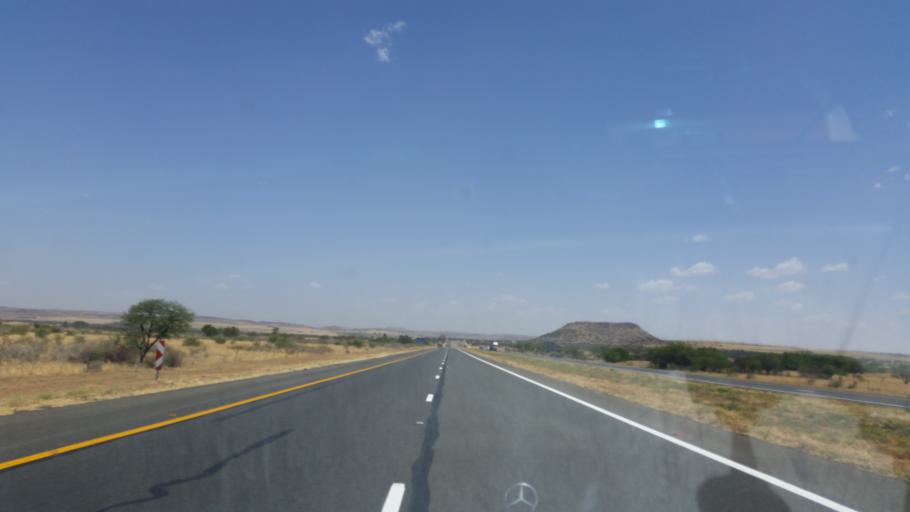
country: ZA
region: Orange Free State
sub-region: Lejweleputswa District Municipality
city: Brandfort
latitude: -28.9414
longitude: 26.4096
